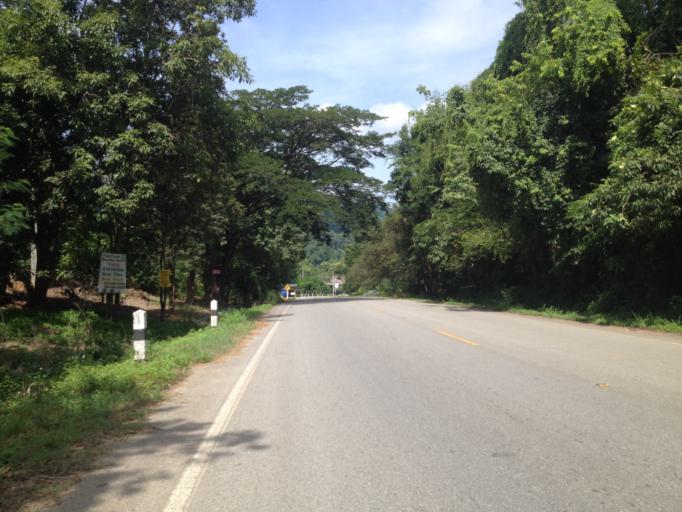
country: TH
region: Chiang Mai
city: Hang Dong
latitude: 18.7756
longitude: 98.8560
